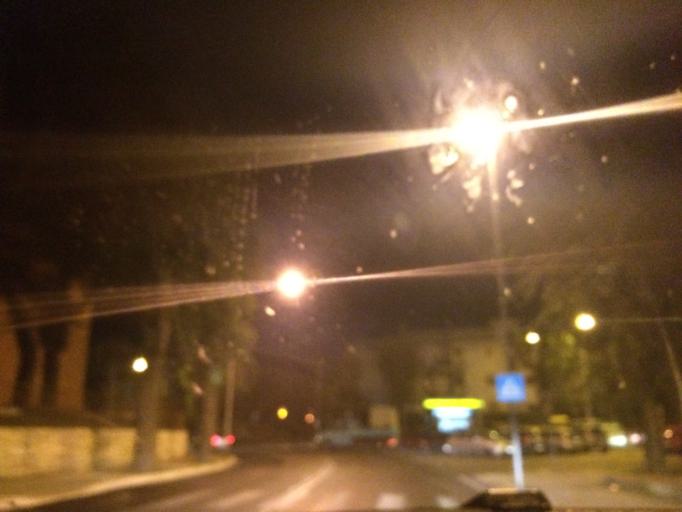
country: IT
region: Basilicate
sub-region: Provincia di Matera
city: Matera
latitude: 40.6652
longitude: 16.5927
